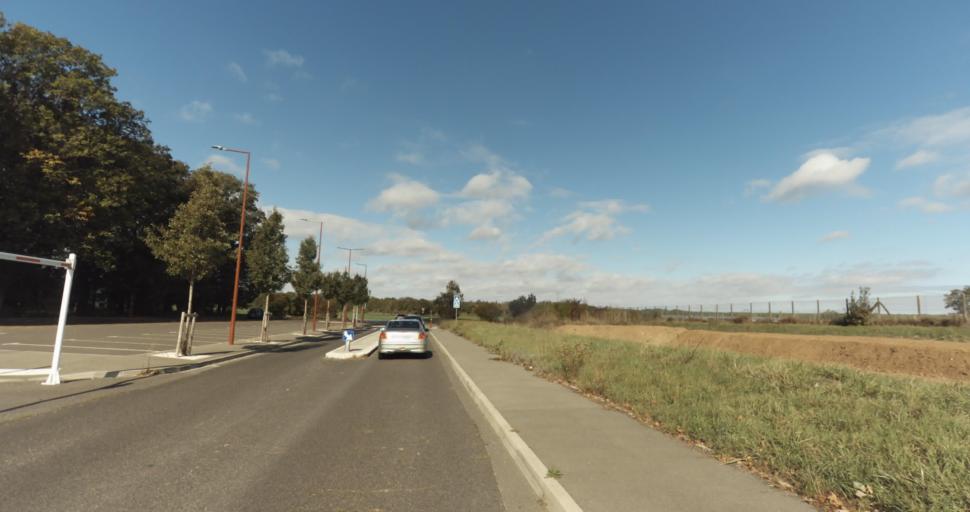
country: FR
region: Centre
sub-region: Departement d'Eure-et-Loir
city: Garnay
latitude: 48.7351
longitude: 1.3302
